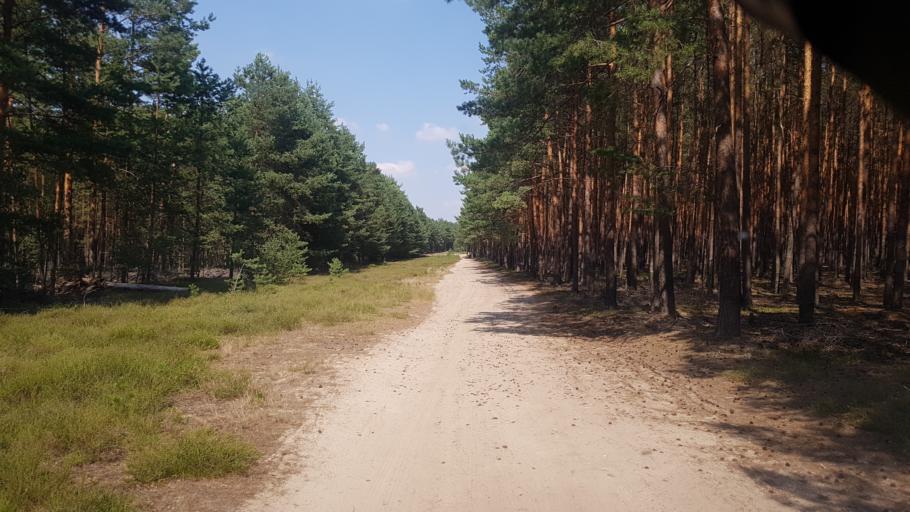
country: DE
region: Brandenburg
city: Spremberg
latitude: 51.6346
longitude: 14.4074
